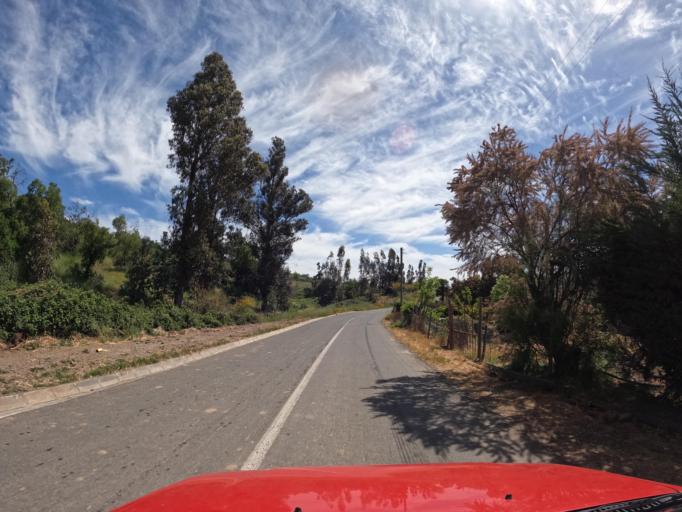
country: CL
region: Maule
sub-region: Provincia de Talca
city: Talca
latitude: -34.9895
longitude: -71.8409
